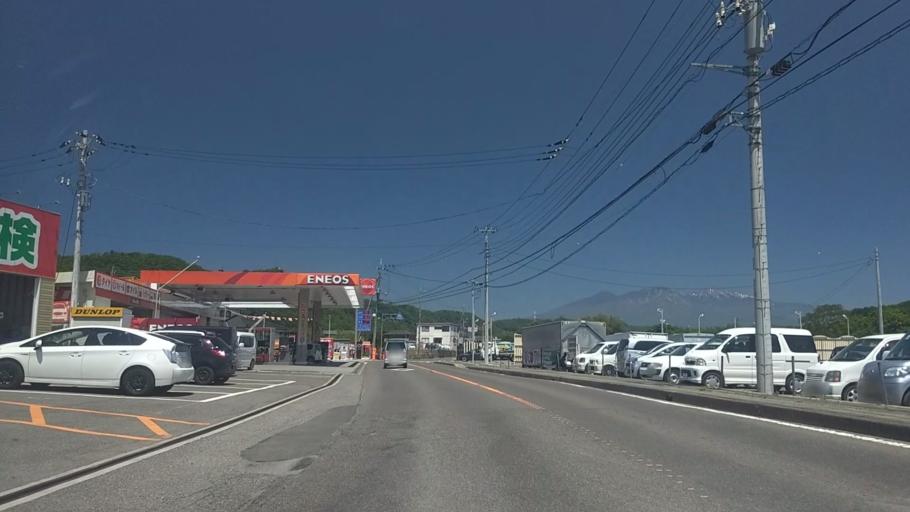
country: JP
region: Yamanashi
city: Nirasaki
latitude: 35.7620
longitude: 138.4296
